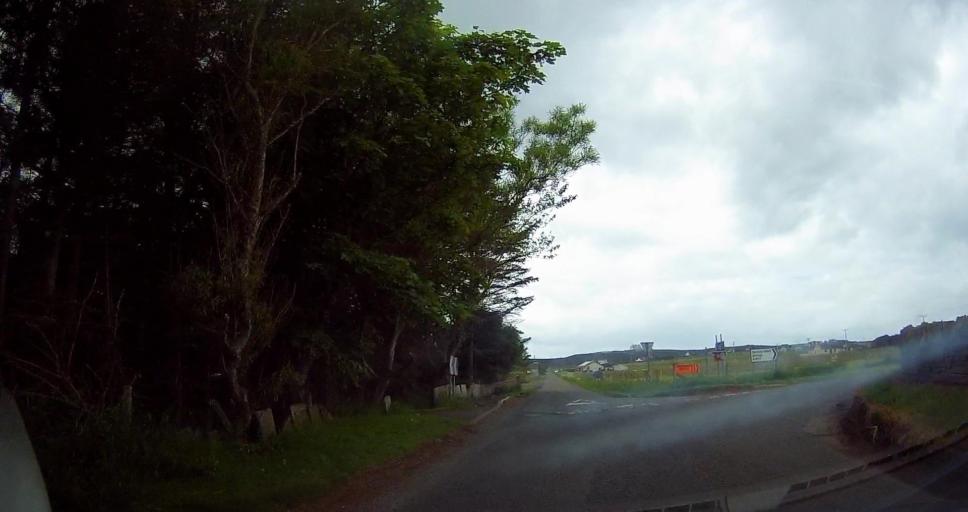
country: GB
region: Scotland
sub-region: Highland
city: Thurso
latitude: 58.6222
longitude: -3.3448
